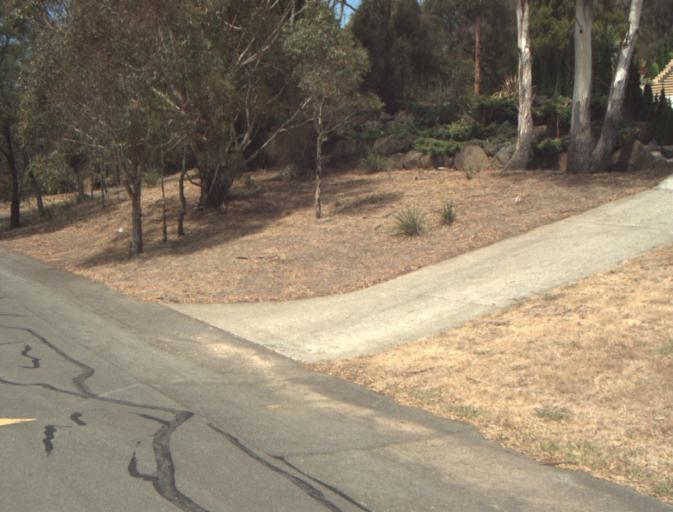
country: AU
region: Tasmania
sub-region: Launceston
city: Summerhill
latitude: -41.4620
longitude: 147.1233
